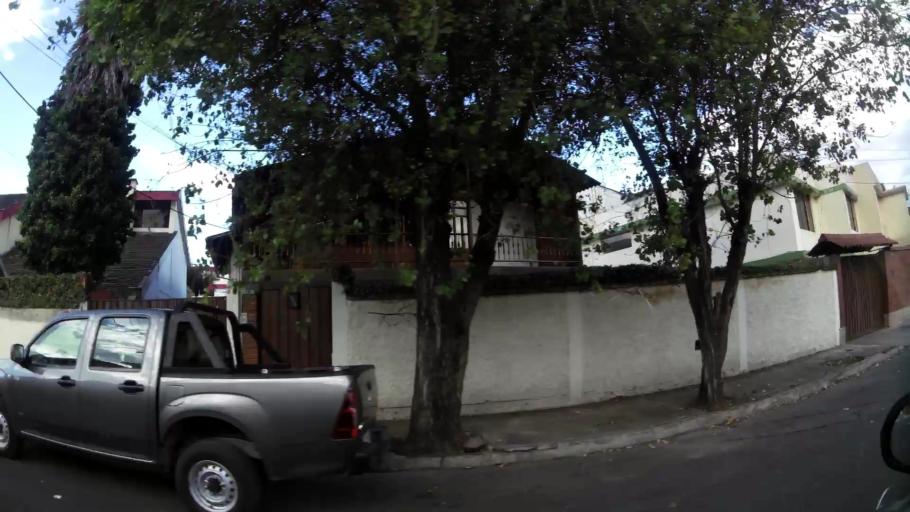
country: EC
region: Pichincha
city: Quito
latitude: -0.1481
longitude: -78.4831
